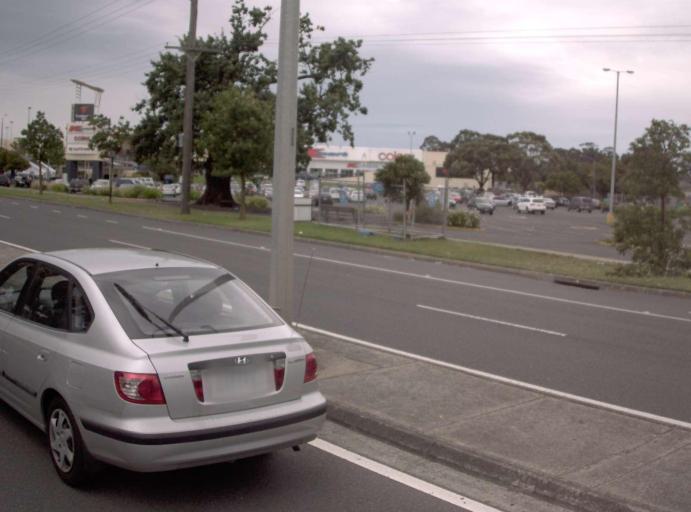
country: AU
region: Victoria
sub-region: Casey
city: Cranbourne
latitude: -38.1064
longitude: 145.2824
